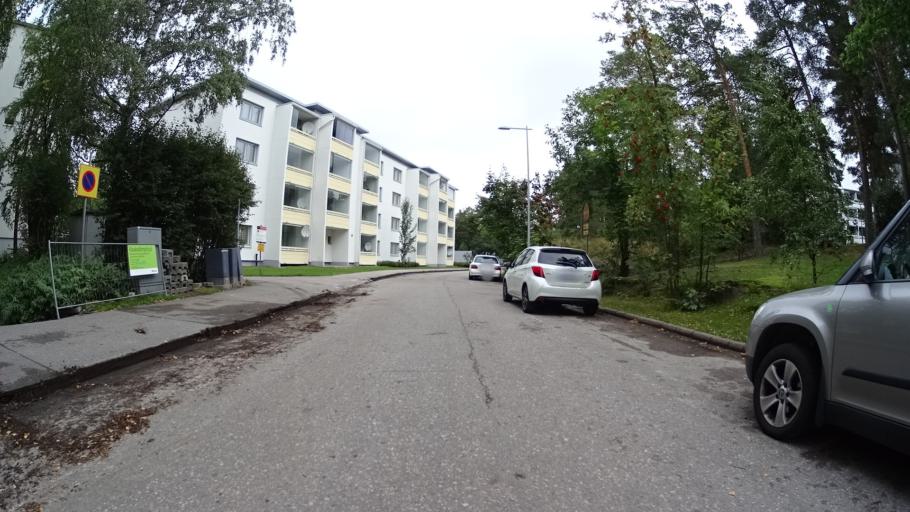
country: FI
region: Uusimaa
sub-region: Helsinki
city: Espoo
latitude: 60.1478
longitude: 24.6511
